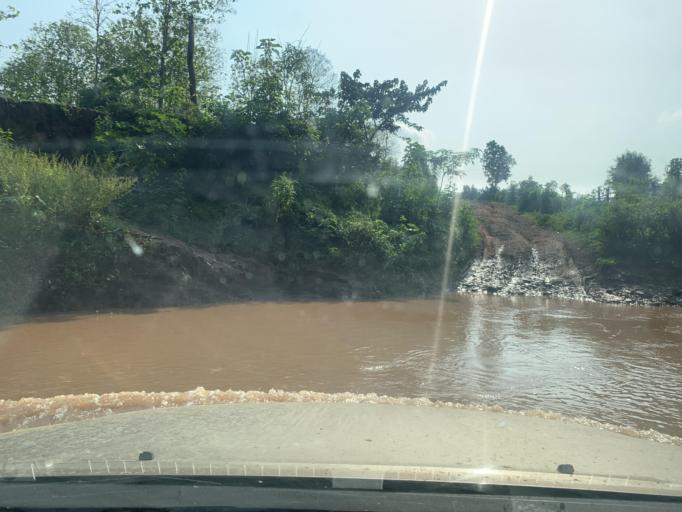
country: TH
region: Uttaradit
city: Ban Khok
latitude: 18.2883
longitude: 101.3241
